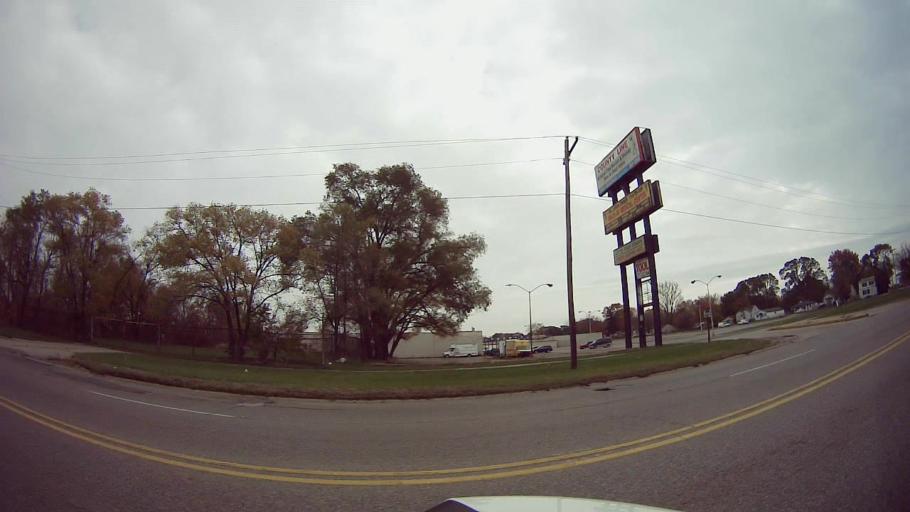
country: US
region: Michigan
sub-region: Oakland County
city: Hazel Park
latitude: 42.4521
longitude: -83.0836
